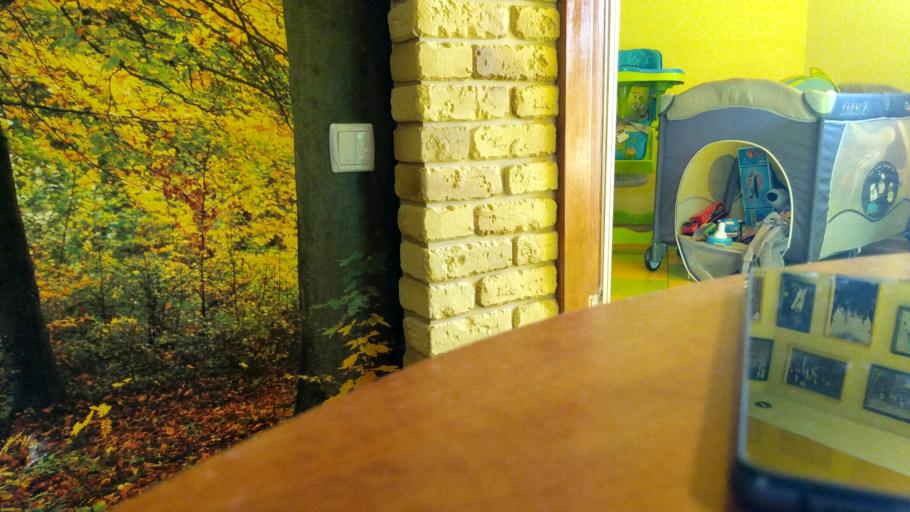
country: RU
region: Tverskaya
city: Likhoslavl'
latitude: 57.2263
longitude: 35.4711
